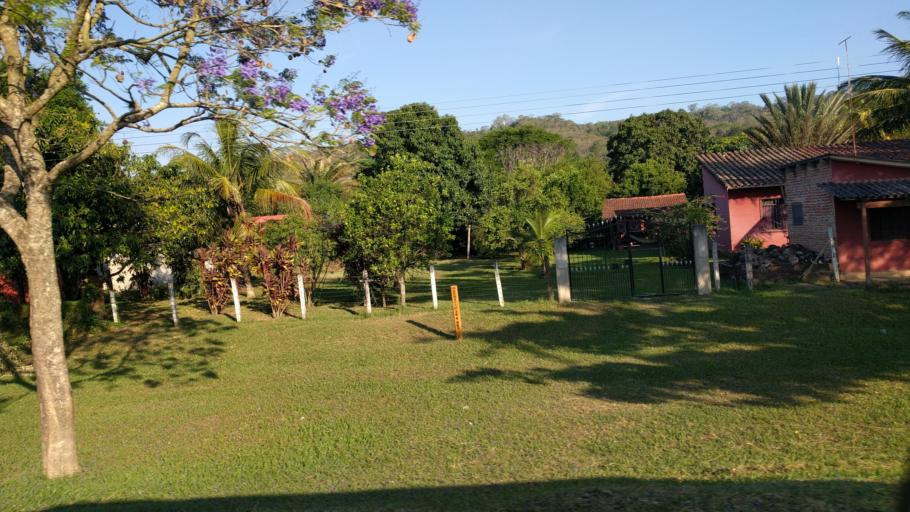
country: BO
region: Santa Cruz
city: Jorochito
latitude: -18.0646
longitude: -63.4355
